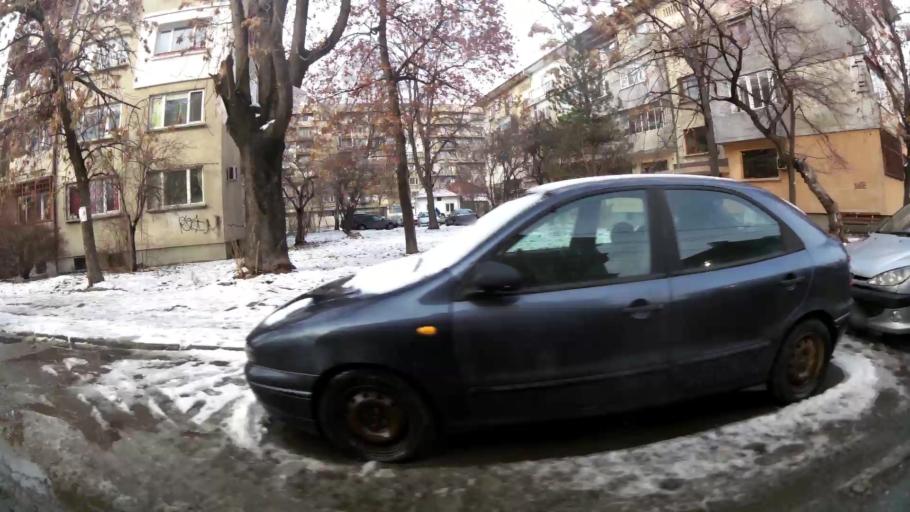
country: BG
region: Sofia-Capital
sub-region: Stolichna Obshtina
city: Sofia
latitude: 42.6987
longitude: 23.3701
